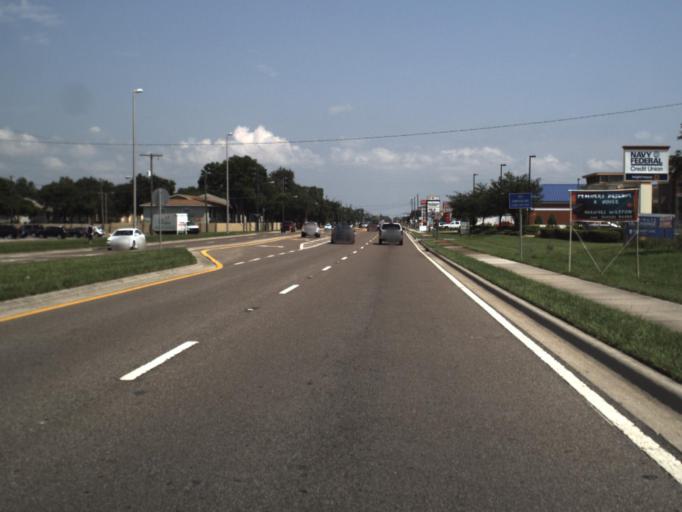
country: US
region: Florida
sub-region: Hillsborough County
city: Tampa
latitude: 27.8994
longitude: -82.5062
